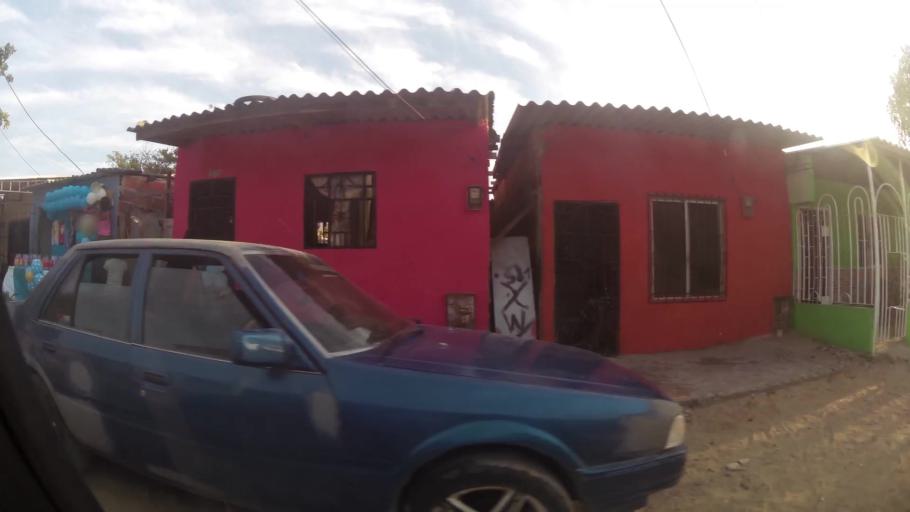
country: CO
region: Atlantico
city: Barranquilla
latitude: 10.9578
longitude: -74.8234
